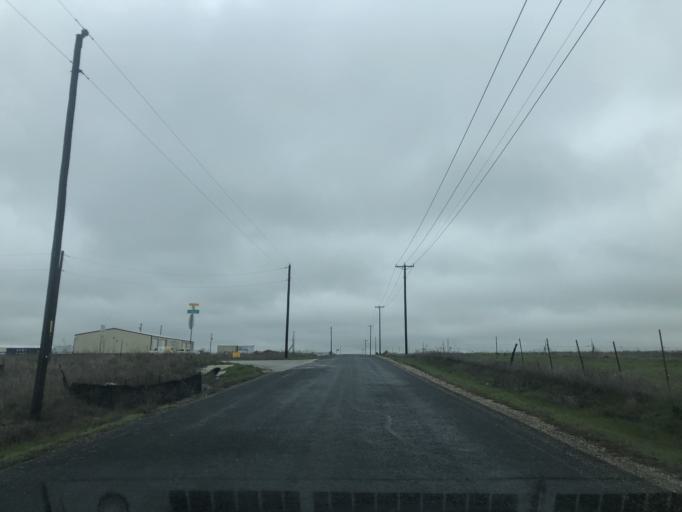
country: US
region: Texas
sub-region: Williamson County
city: Serenada
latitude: 30.7699
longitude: -97.6175
